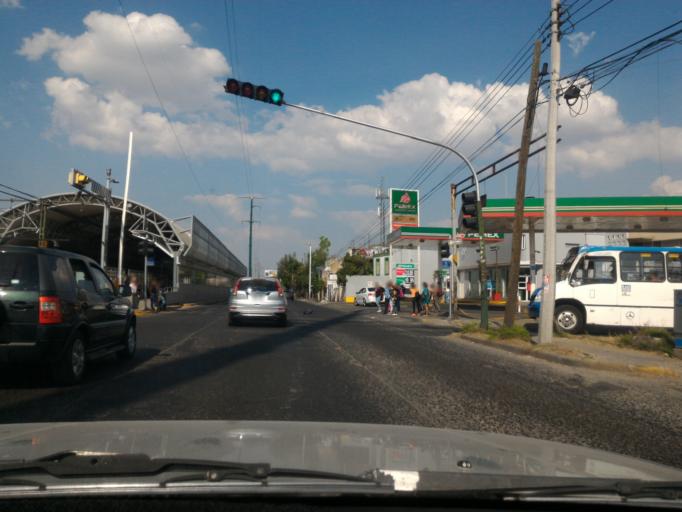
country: MX
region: Jalisco
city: Guadalajara
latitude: 20.6319
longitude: -103.3811
